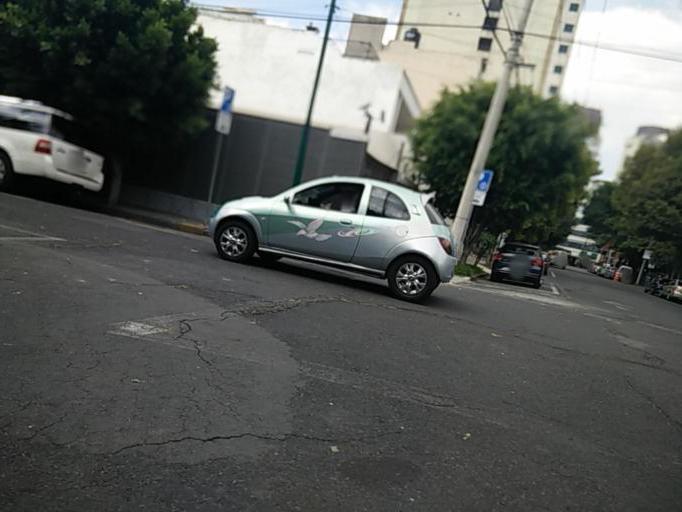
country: MX
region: Mexico City
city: Miguel Hidalgo
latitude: 19.4305
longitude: -99.1793
